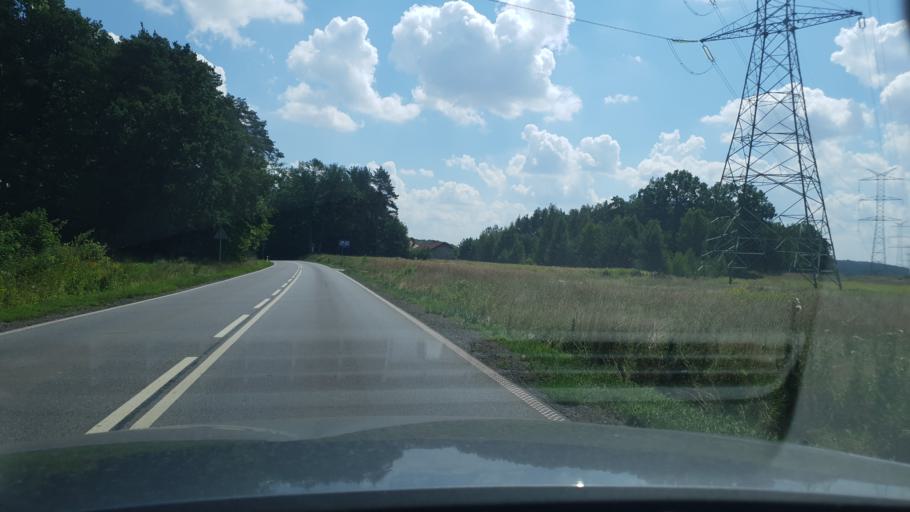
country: PL
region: Kujawsko-Pomorskie
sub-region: Grudziadz
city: Grudziadz
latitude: 53.4451
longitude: 18.8154
